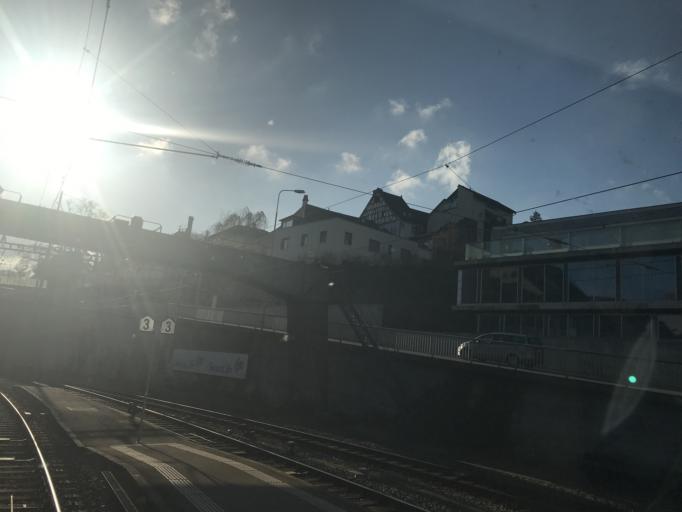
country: CH
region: Schaffhausen
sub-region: Bezirk Schaffhausen
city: Schaffhausen
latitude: 47.6973
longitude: 8.6315
